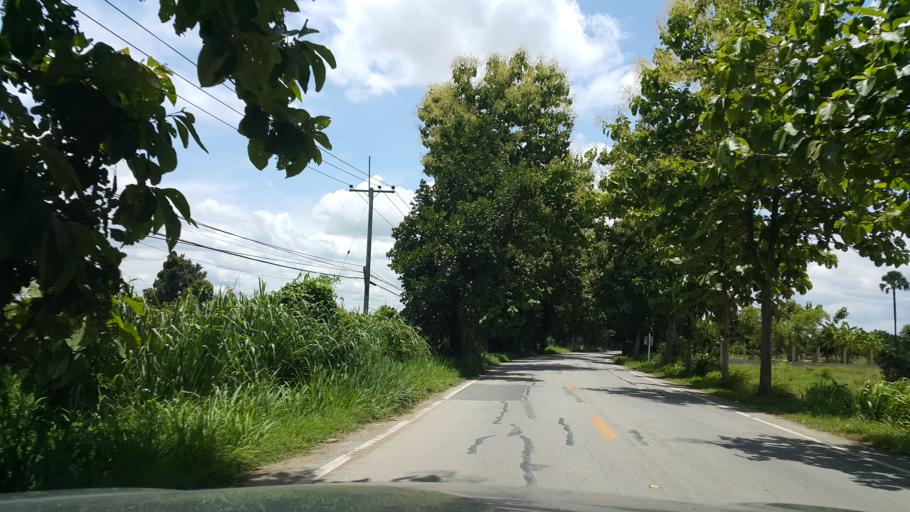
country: TH
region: Chiang Mai
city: San Kamphaeng
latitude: 18.7255
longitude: 99.1607
